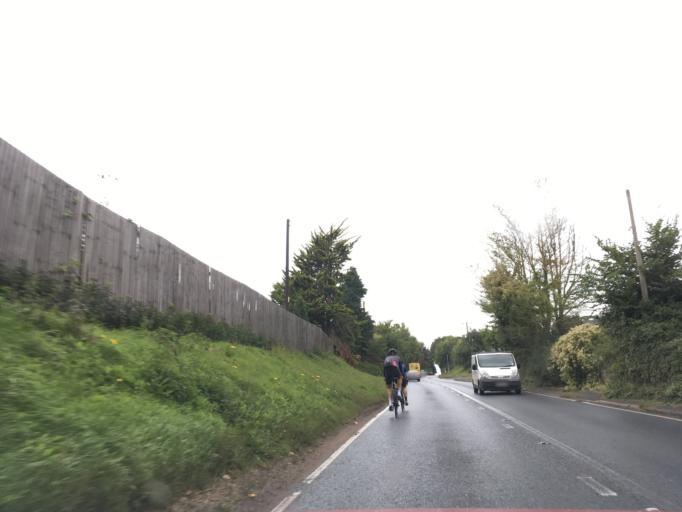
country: GB
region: England
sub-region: Herefordshire
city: Lea
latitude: 51.8928
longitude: -2.5012
